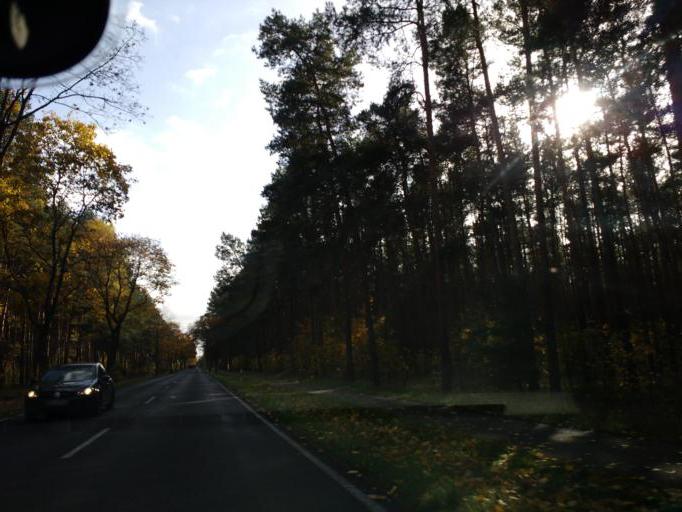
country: DE
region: Brandenburg
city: Grunheide
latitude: 52.3861
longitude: 13.8286
